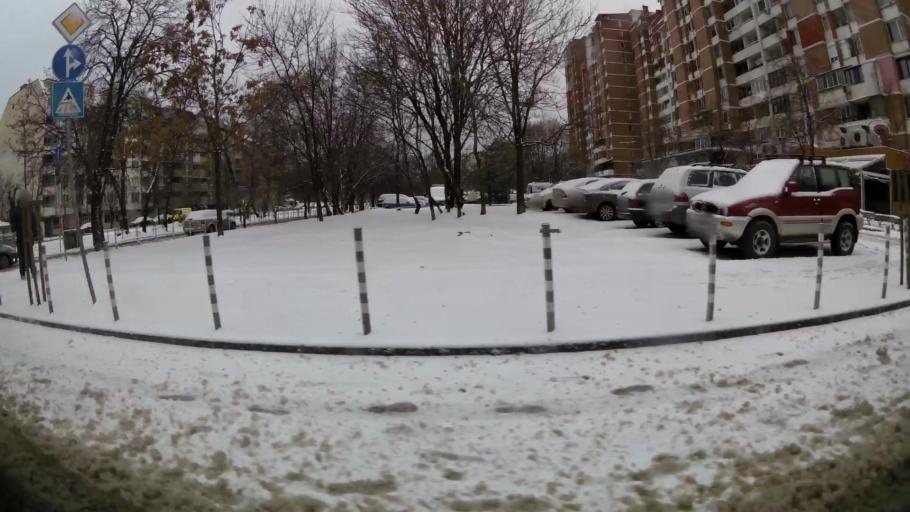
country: BG
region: Sofia-Capital
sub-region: Stolichna Obshtina
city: Sofia
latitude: 42.7043
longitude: 23.3040
